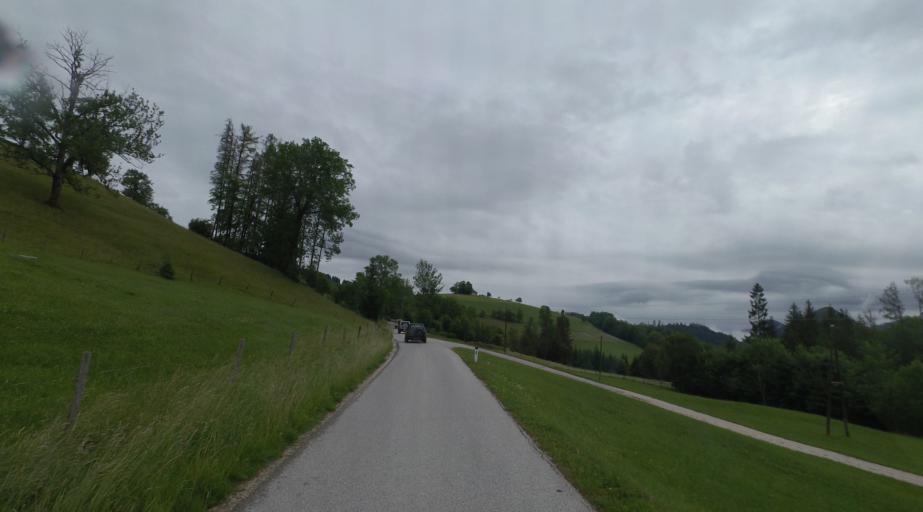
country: AT
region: Upper Austria
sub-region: Politischer Bezirk Kirchdorf an der Krems
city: Micheldorf in Oberoesterreich
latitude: 47.8955
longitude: 14.1590
